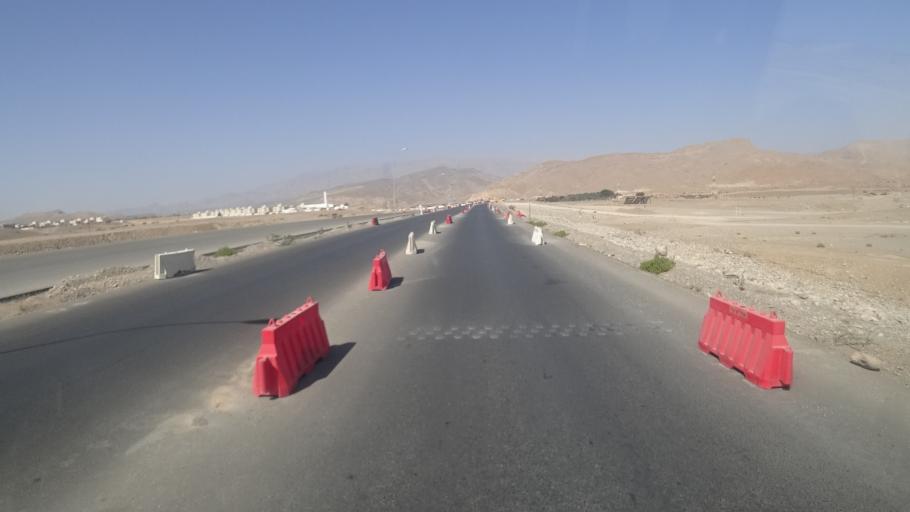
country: OM
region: Ash Sharqiyah
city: Sur
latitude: 22.5173
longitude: 59.4509
